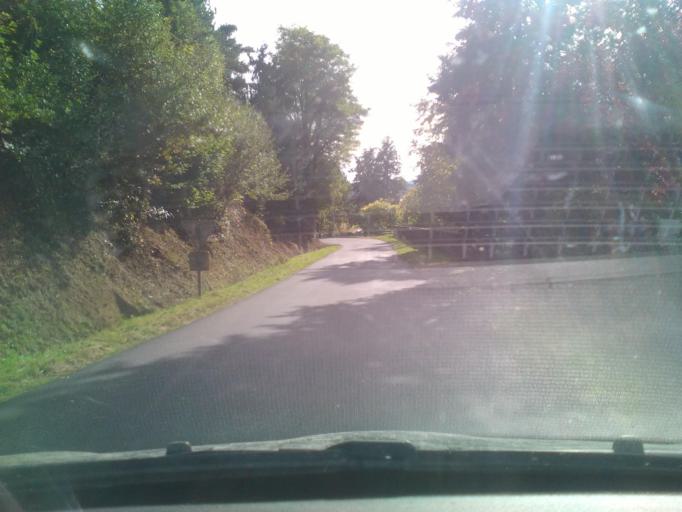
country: FR
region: Lorraine
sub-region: Departement des Vosges
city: Sainte-Marguerite
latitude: 48.2783
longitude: 6.9846
